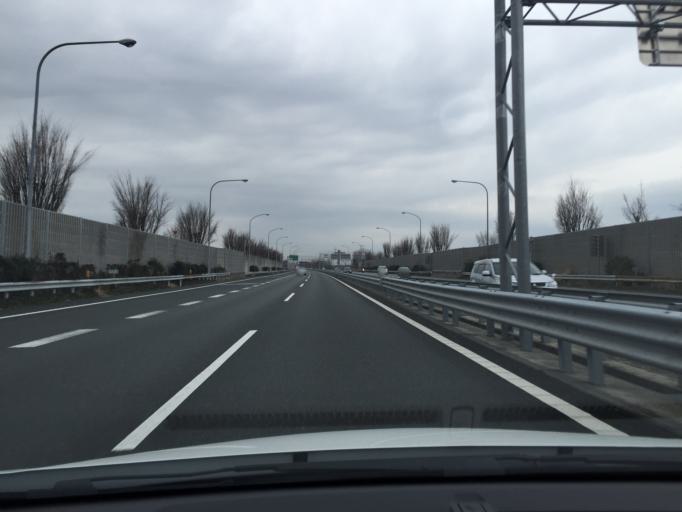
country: JP
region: Saitama
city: Sakado
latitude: 35.9298
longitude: 139.3988
